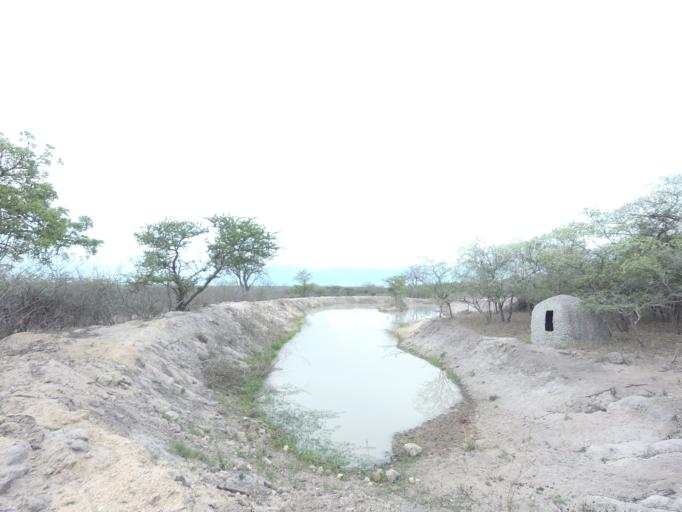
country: ZA
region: Limpopo
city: Thulamahashi
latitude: -24.5282
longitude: 31.1132
